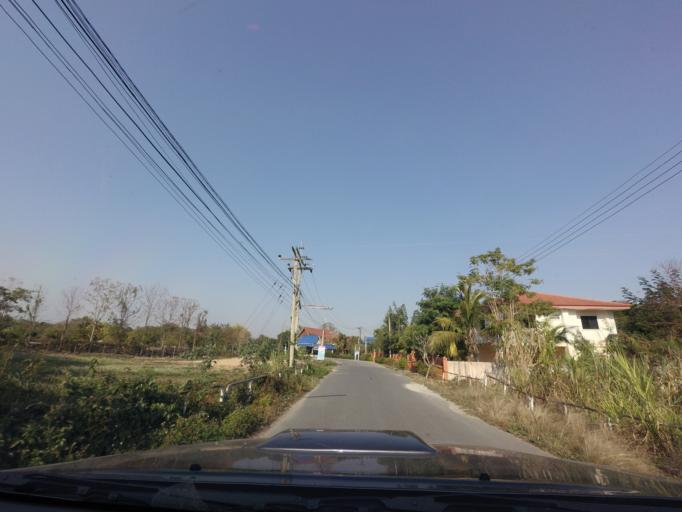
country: TH
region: Chiang Mai
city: San Sai
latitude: 18.9216
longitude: 98.9631
